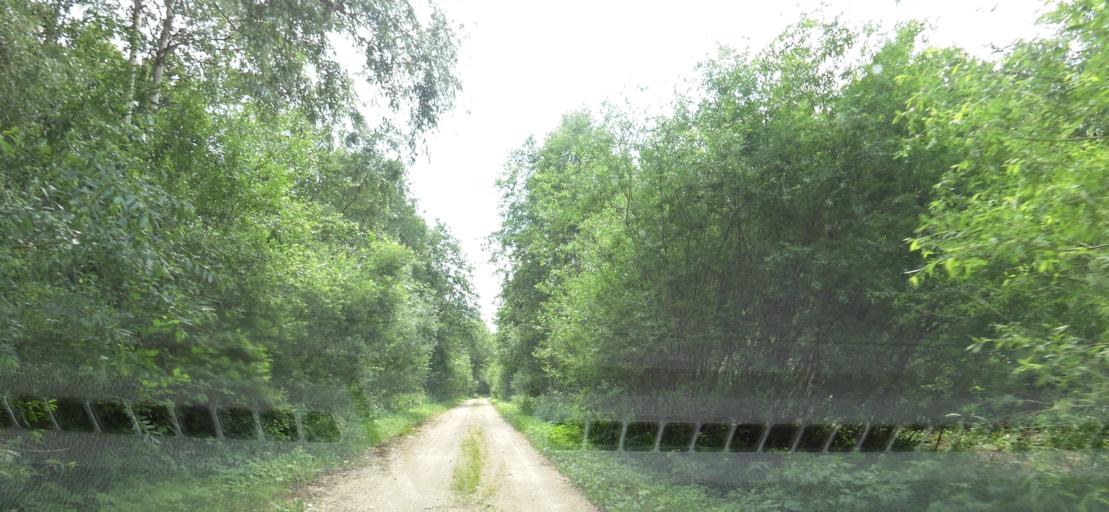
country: LV
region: Ogre
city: Jumprava
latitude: 56.4412
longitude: 24.9077
